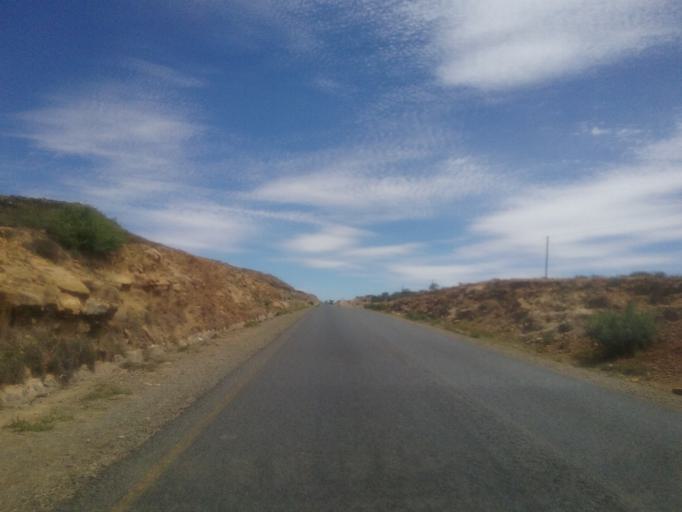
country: LS
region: Mohale's Hoek District
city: Mohale's Hoek
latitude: -30.0705
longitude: 27.4233
